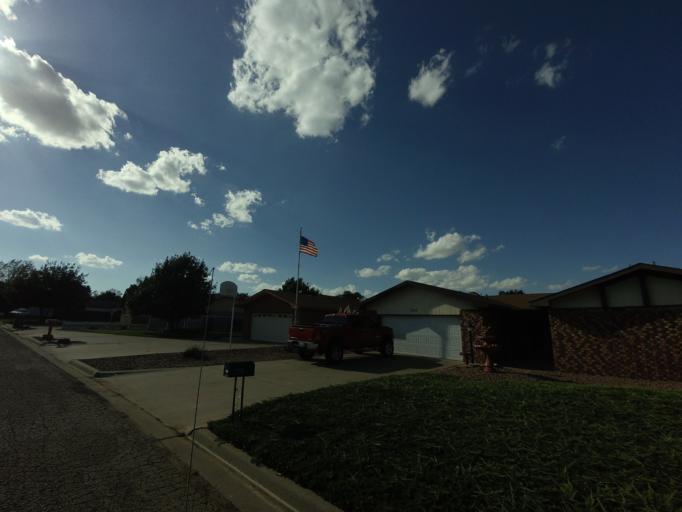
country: US
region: New Mexico
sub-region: Curry County
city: Clovis
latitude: 34.4354
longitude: -103.1807
